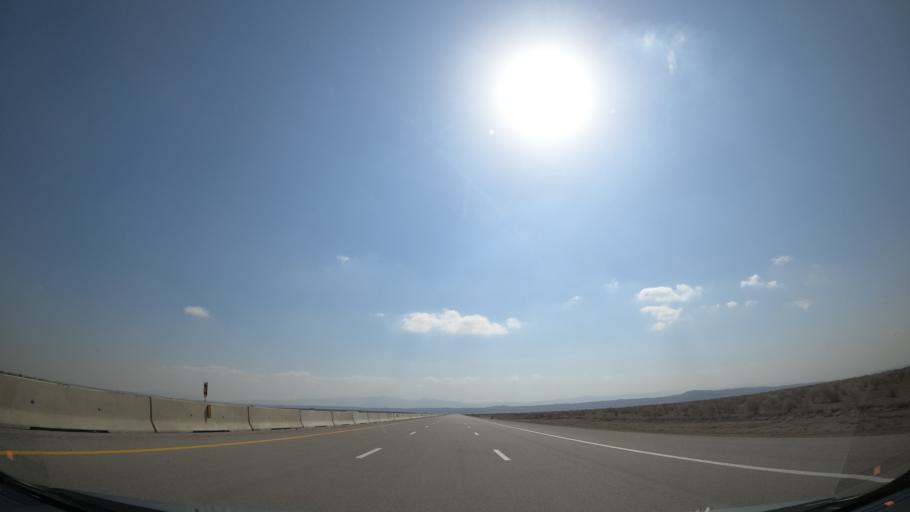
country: IR
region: Alborz
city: Nazarabad
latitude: 35.8541
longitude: 50.4803
